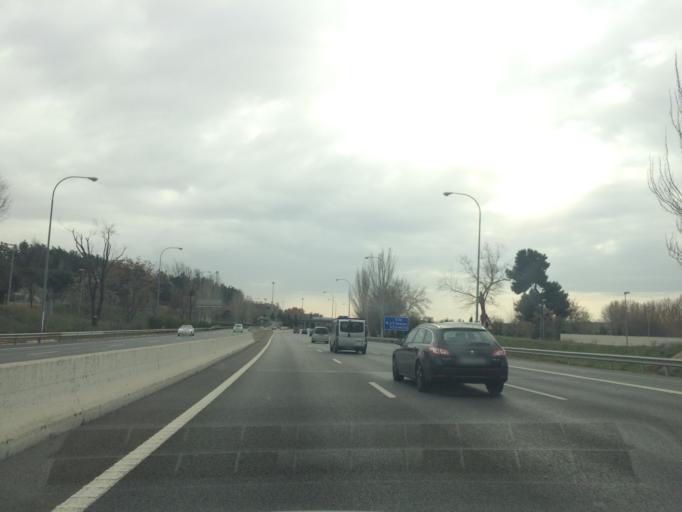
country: ES
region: Madrid
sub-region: Provincia de Madrid
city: Moncloa-Aravaca
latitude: 40.4484
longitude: -3.7412
